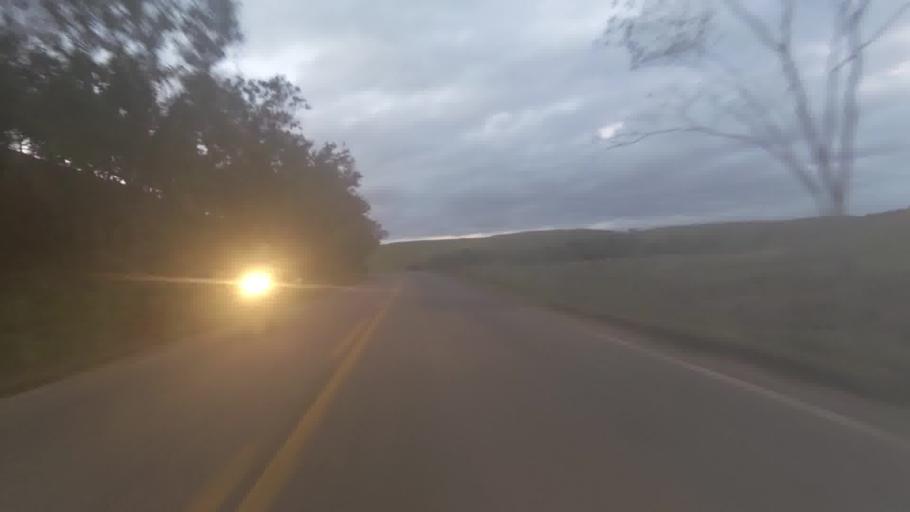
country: BR
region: Espirito Santo
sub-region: Itapemirim
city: Itapemirim
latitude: -20.9610
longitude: -40.8741
